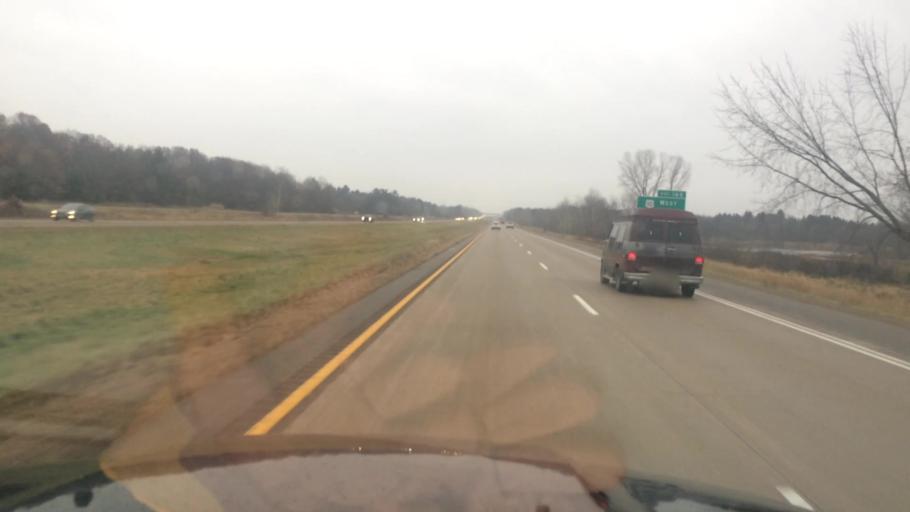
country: US
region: Wisconsin
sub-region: Portage County
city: Stevens Point
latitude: 44.6164
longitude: -89.6266
